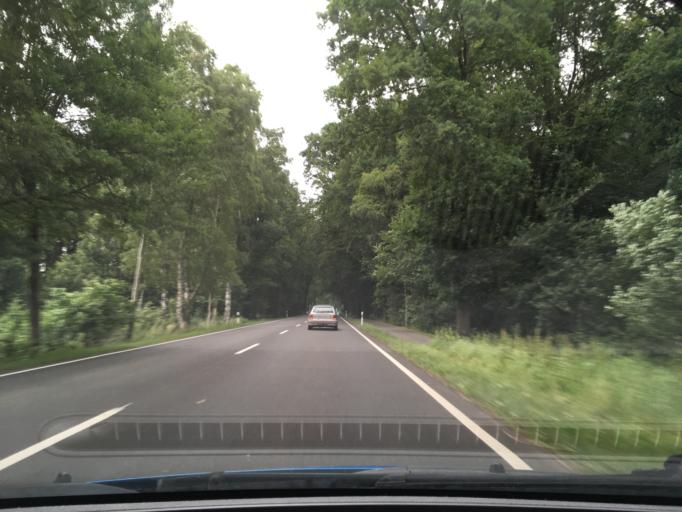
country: DE
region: Lower Saxony
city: Wenzendorf
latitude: 53.3526
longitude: 9.8087
